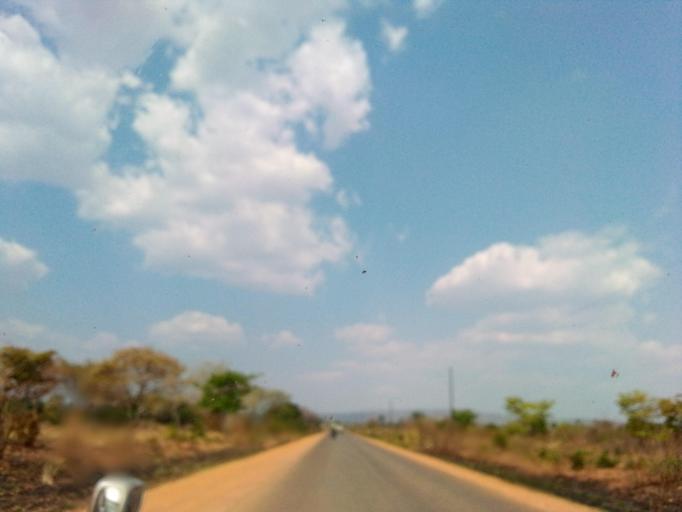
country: ZM
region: Northern
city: Mpika
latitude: -11.8329
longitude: 31.4122
